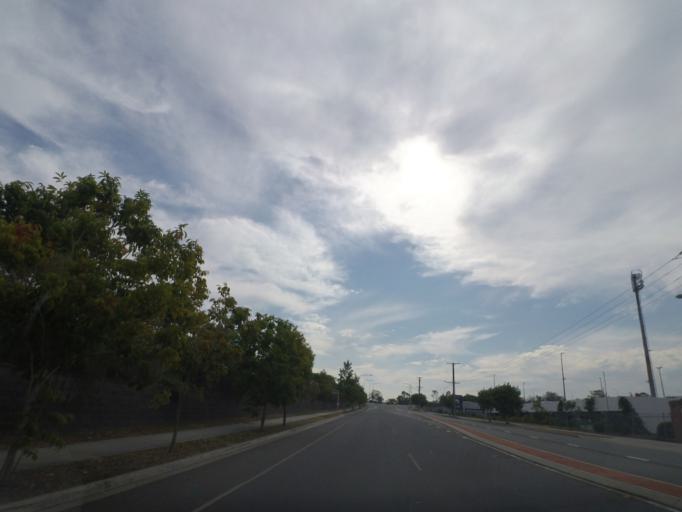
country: AU
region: Queensland
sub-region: Brisbane
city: Richlands
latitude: -27.5937
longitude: 152.9506
